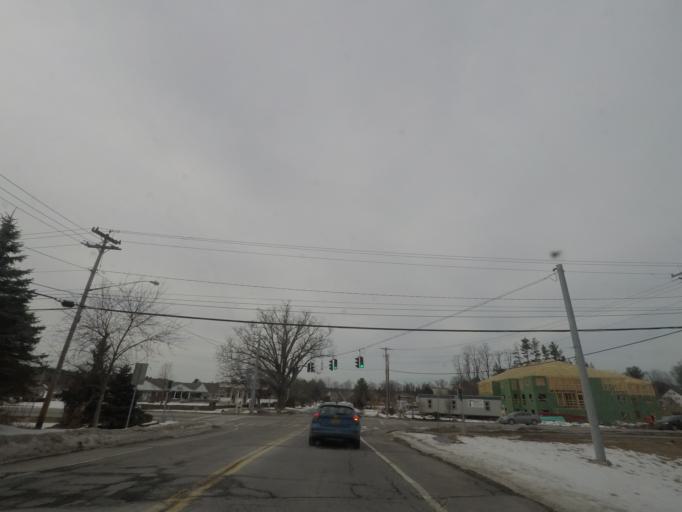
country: US
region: New York
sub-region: Albany County
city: Westmere
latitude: 42.6824
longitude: -73.9026
